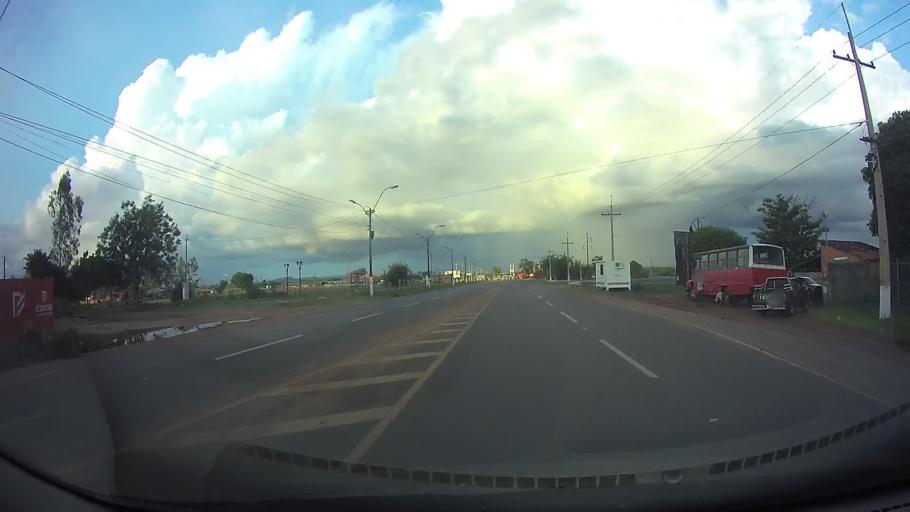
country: PY
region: Paraguari
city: Carapegua
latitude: -25.7644
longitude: -57.2351
